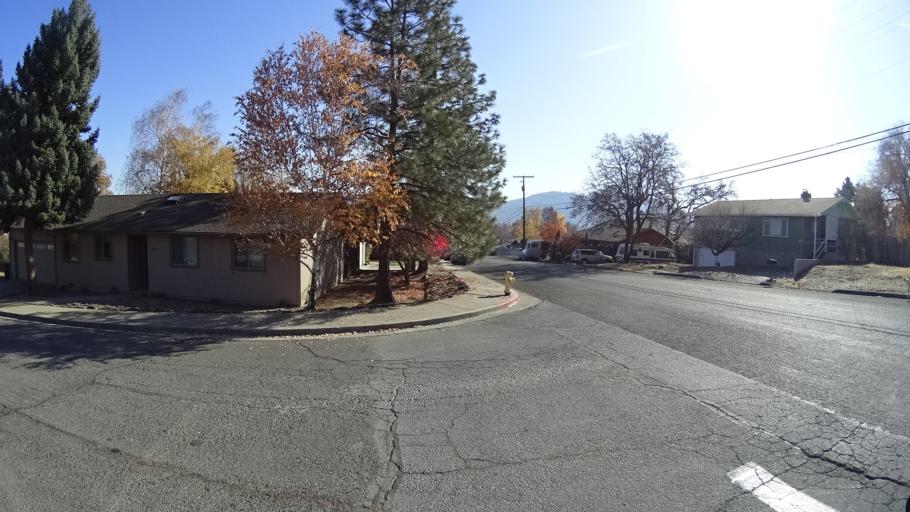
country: US
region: California
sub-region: Siskiyou County
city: Yreka
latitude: 41.7353
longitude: -122.6479
